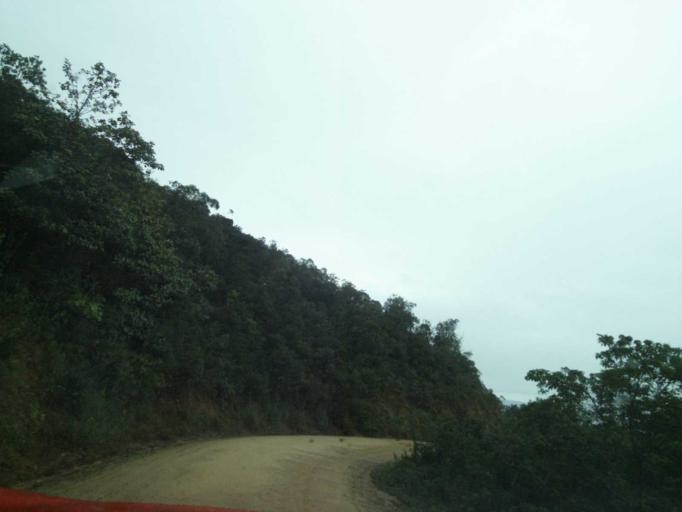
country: BR
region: Santa Catarina
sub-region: Anitapolis
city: Anitapolis
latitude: -27.9212
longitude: -49.1792
